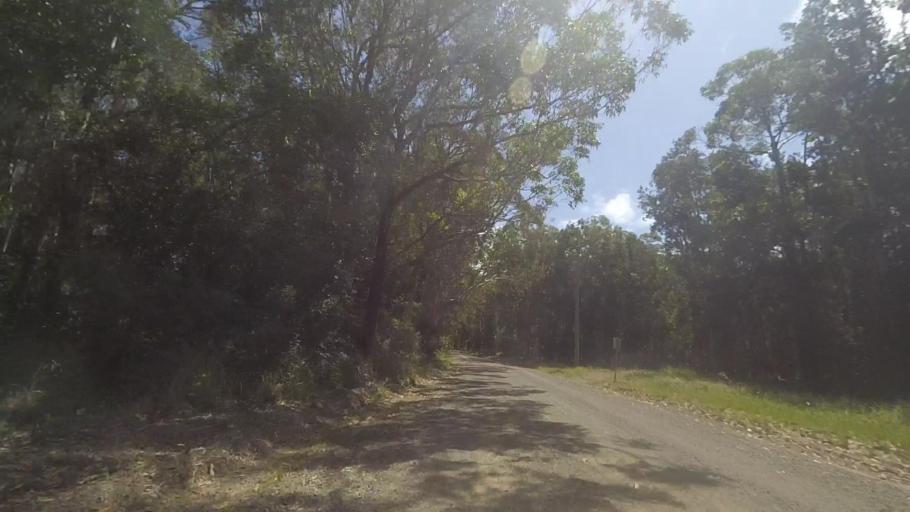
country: AU
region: New South Wales
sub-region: Great Lakes
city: Bulahdelah
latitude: -32.5093
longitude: 152.2947
